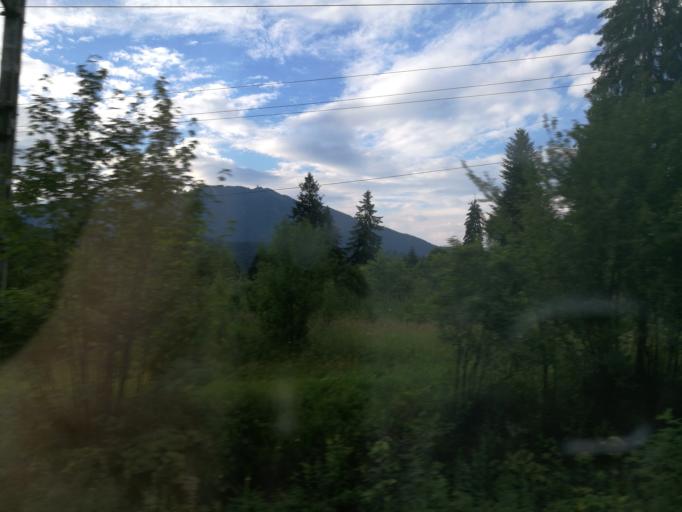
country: RO
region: Brasov
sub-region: Oras Predeal
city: Predeal
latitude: 45.5235
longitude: 25.5806
